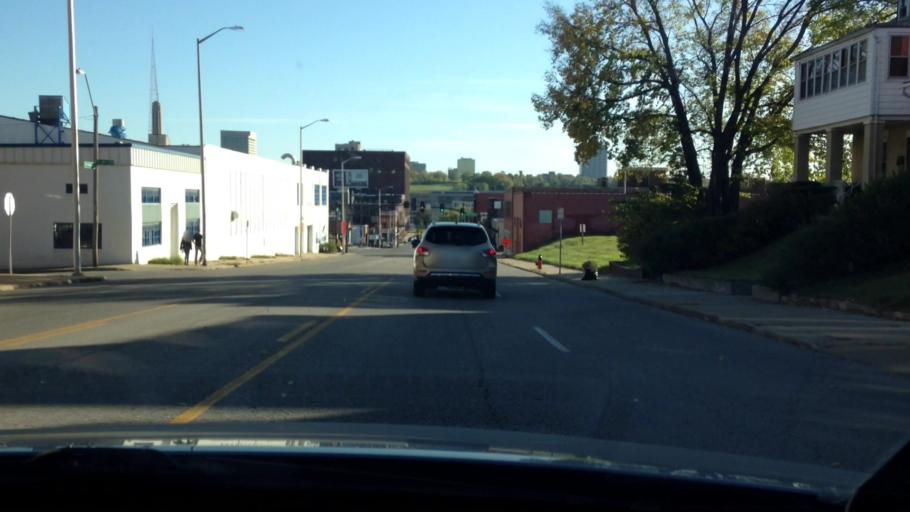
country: US
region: Missouri
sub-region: Jackson County
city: Kansas City
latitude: 39.0905
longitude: -94.5889
